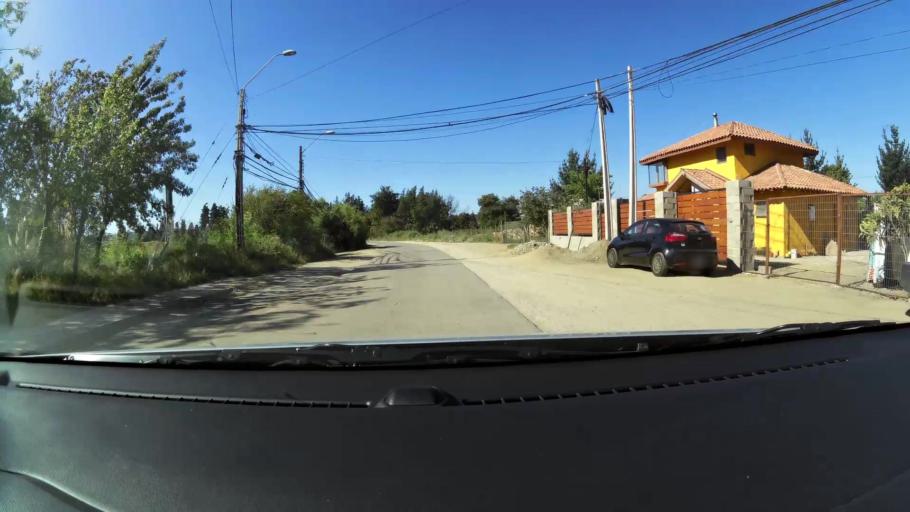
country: CL
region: Valparaiso
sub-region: Provincia de Valparaiso
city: Vina del Mar
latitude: -33.1367
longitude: -71.5638
